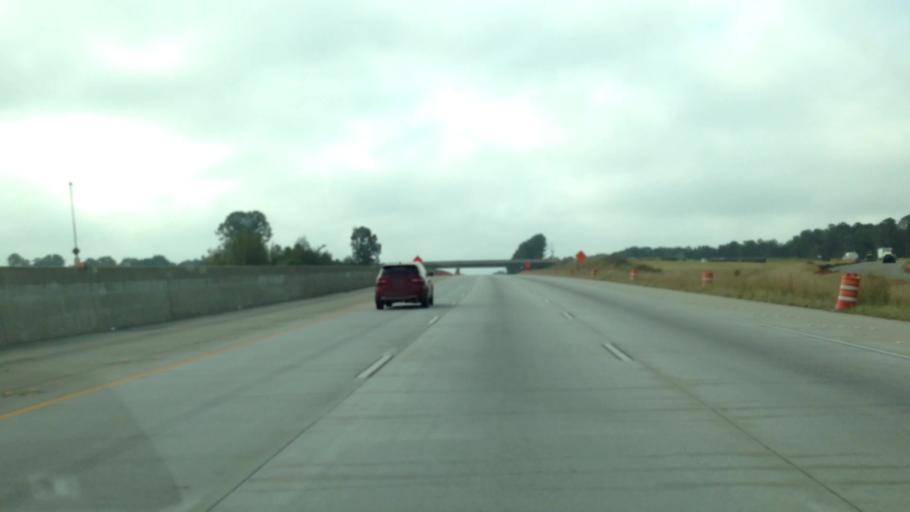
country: US
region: Georgia
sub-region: Coweta County
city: East Newnan
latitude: 33.3640
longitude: -84.7601
